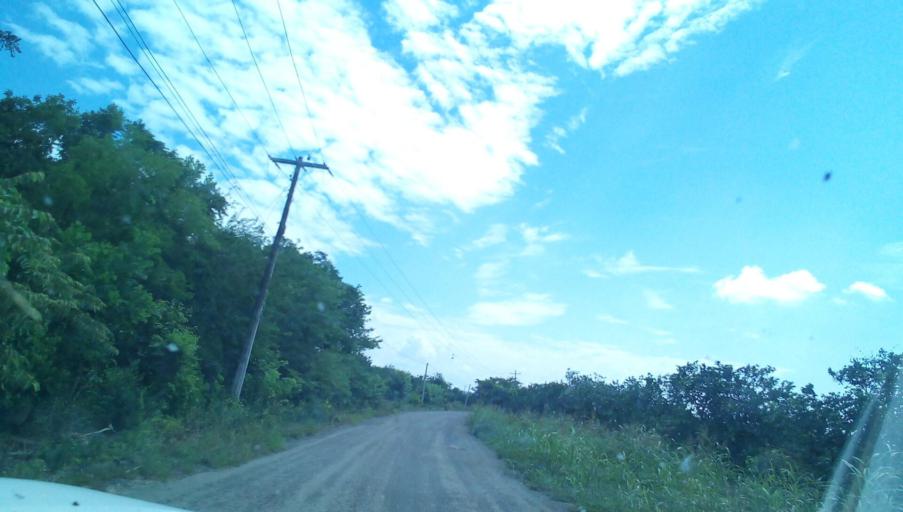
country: MX
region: Veracruz
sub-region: Alamo Temapache
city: Vegas de la Soledad y Soledad Dos
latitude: 20.9030
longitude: -97.9400
